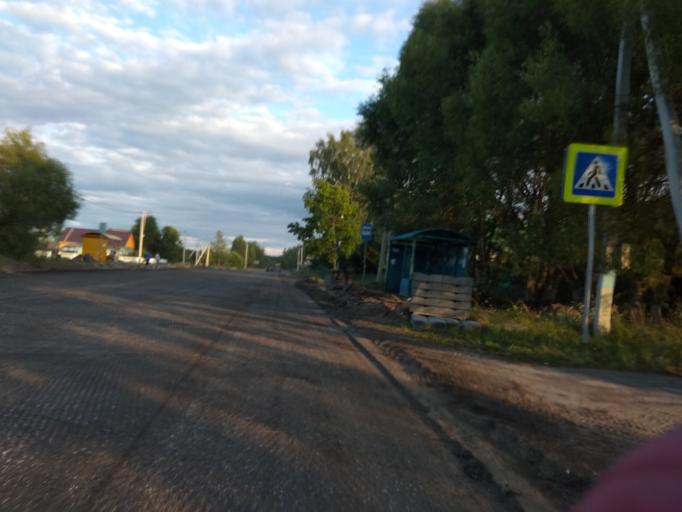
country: RU
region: Moskovskaya
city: Misheronskiy
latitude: 55.6497
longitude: 39.7560
